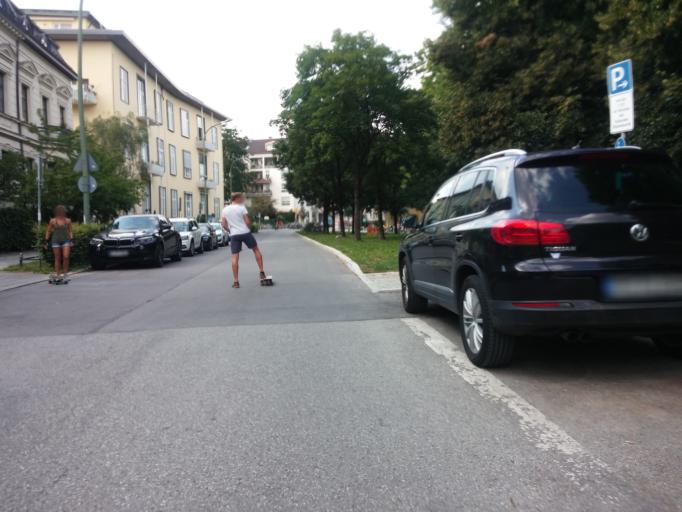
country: DE
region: Bavaria
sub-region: Upper Bavaria
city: Munich
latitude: 48.1490
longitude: 11.5848
